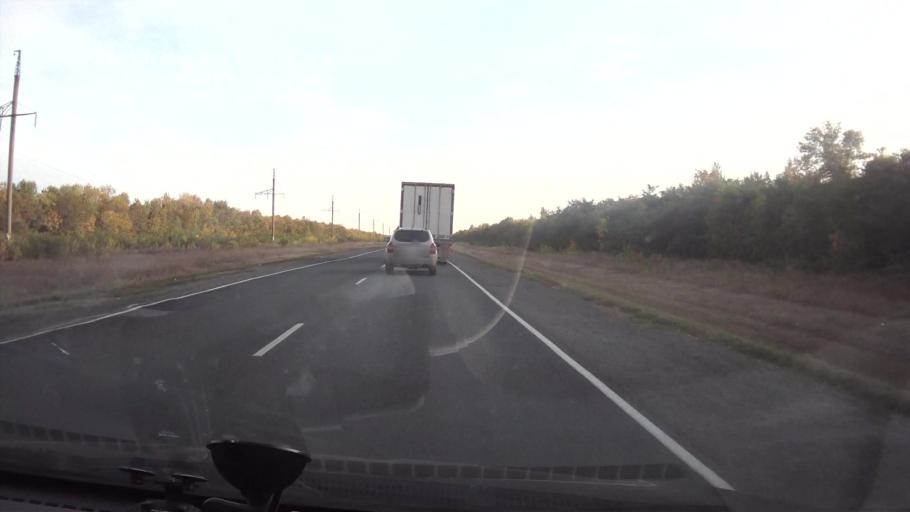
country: RU
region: Saratov
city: Krasnoarmeysk
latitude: 51.1246
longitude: 45.6506
